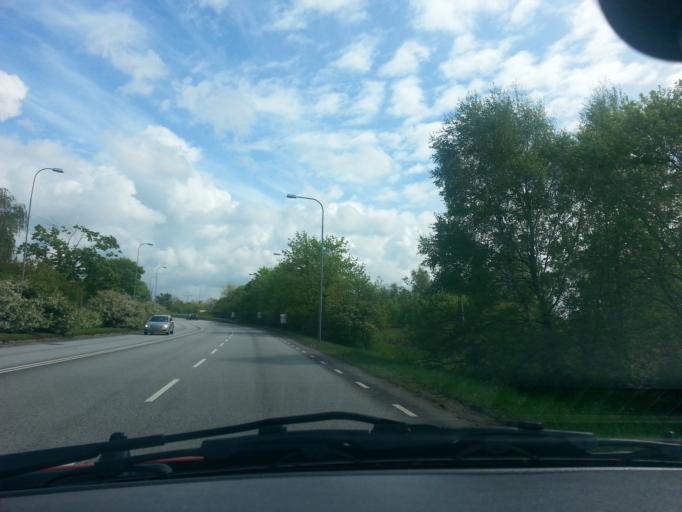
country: SE
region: Vaestra Goetaland
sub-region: Goteborg
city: Goeteborg
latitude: 57.7271
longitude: 11.9654
